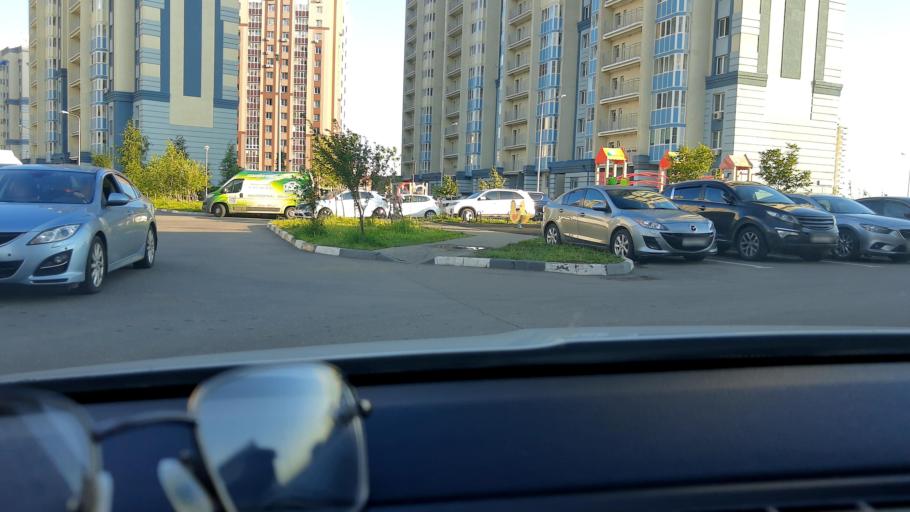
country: RU
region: Moskovskaya
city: Domodedovo
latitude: 55.4046
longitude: 37.7664
